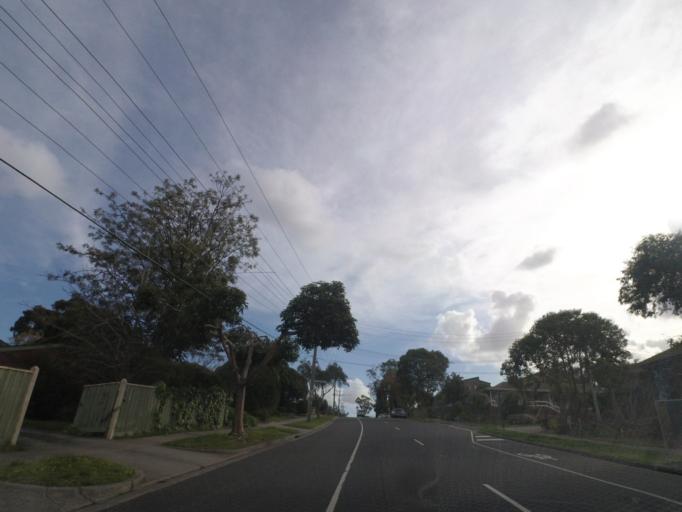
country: AU
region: Victoria
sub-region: Whitehorse
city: Vermont South
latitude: -37.8476
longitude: 145.1836
